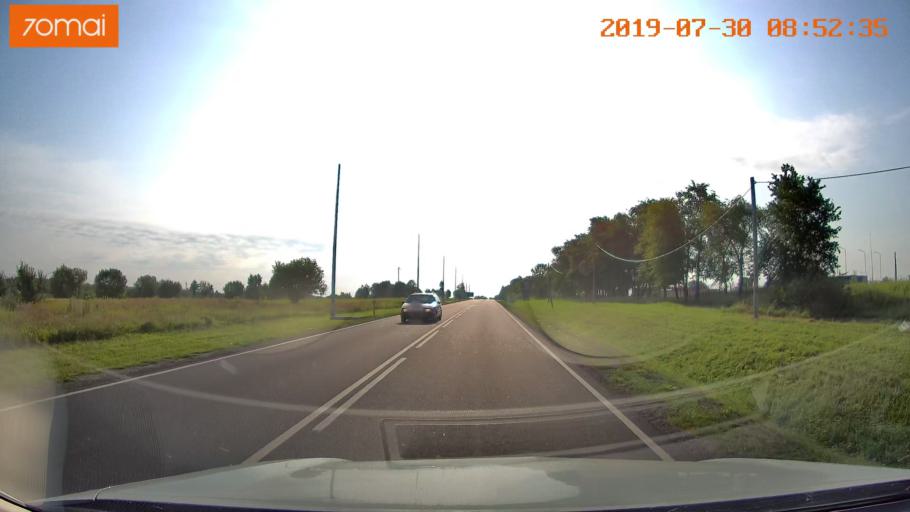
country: RU
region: Kaliningrad
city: Chernyakhovsk
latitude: 54.6031
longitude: 21.9755
